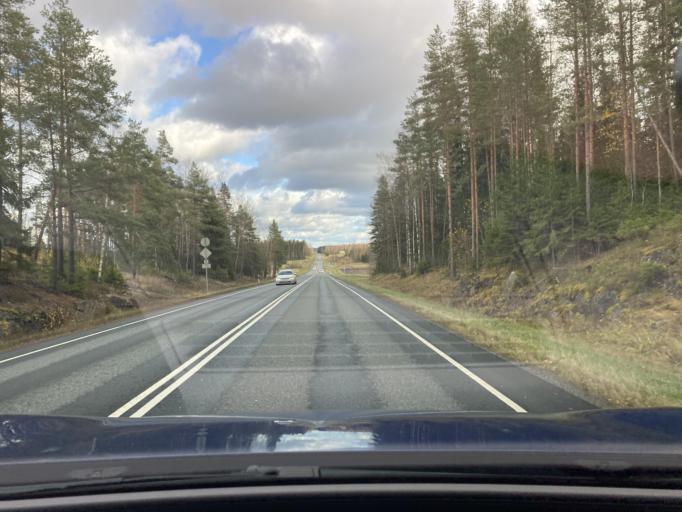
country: FI
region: Haeme
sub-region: Forssa
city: Humppila
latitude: 60.9405
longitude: 23.2818
